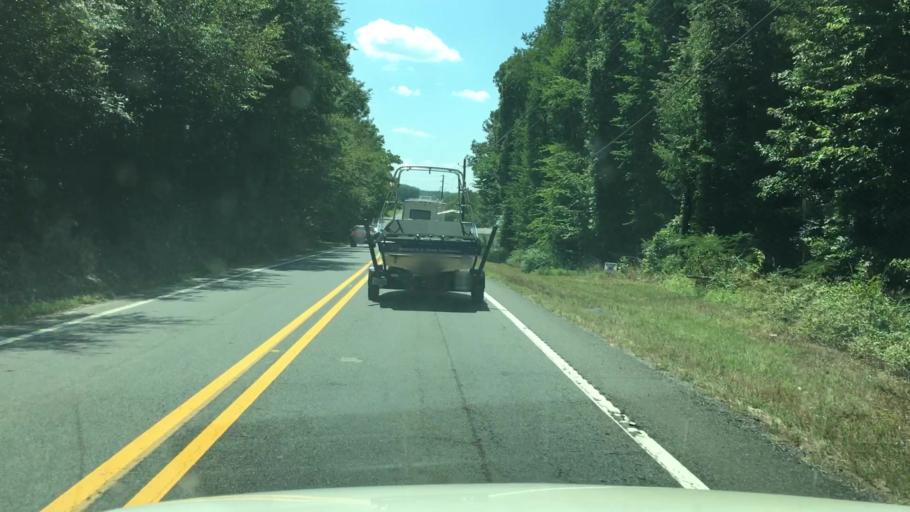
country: US
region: Arkansas
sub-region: Garland County
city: Piney
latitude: 34.5096
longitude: -93.1741
